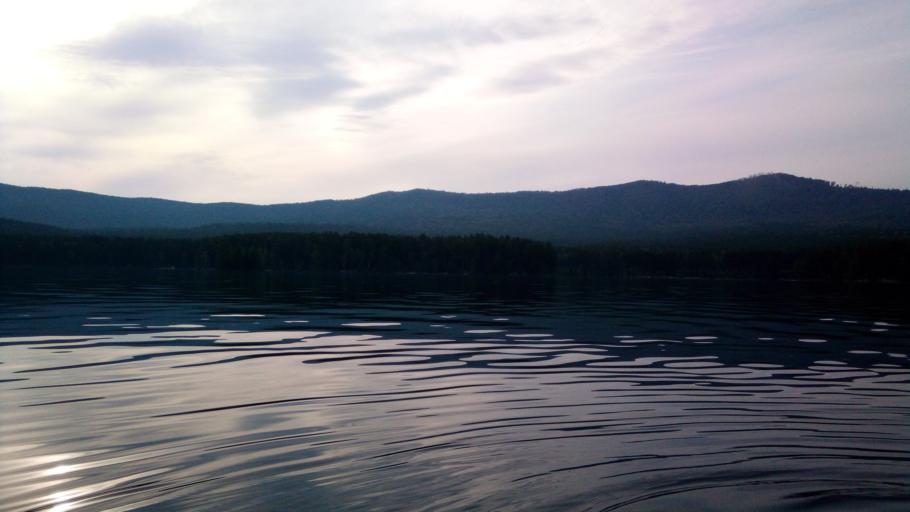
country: RU
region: Chelyabinsk
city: Turgoyak
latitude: 55.1730
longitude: 60.0293
